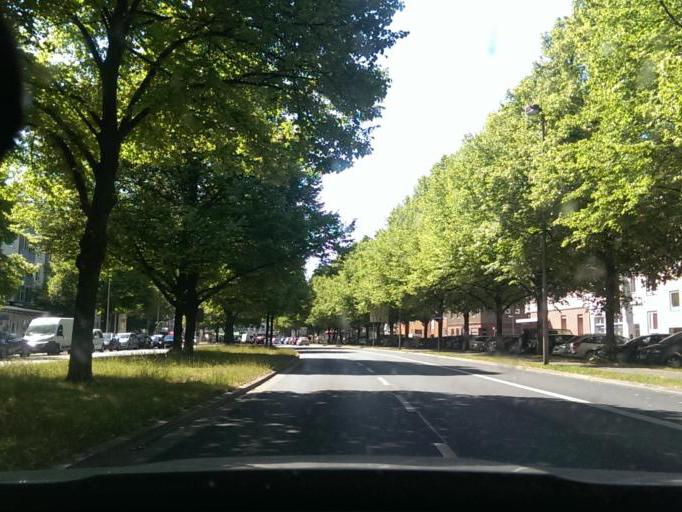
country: DE
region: Lower Saxony
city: Hannover
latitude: 52.3719
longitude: 9.7518
